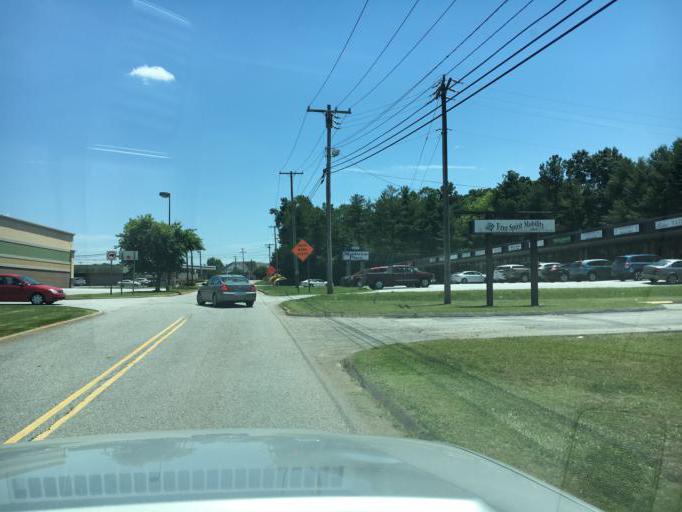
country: US
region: South Carolina
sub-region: Greenville County
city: Greer
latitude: 34.9442
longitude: -82.2491
